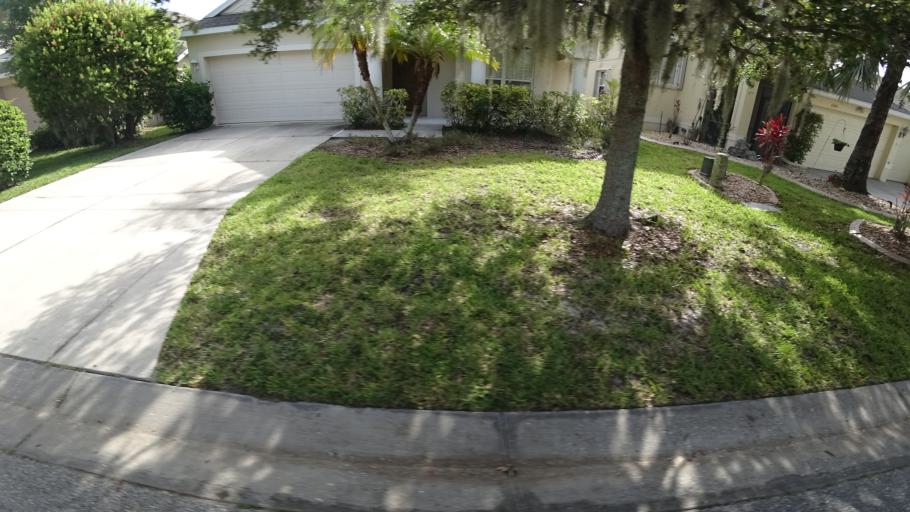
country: US
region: Florida
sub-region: Manatee County
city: Ellenton
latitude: 27.5556
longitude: -82.5004
